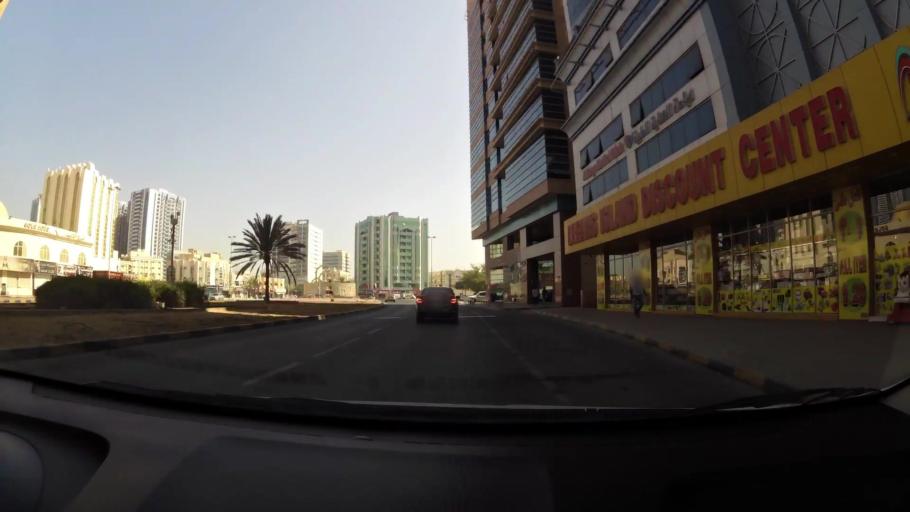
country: AE
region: Ajman
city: Ajman
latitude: 25.4123
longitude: 55.4440
